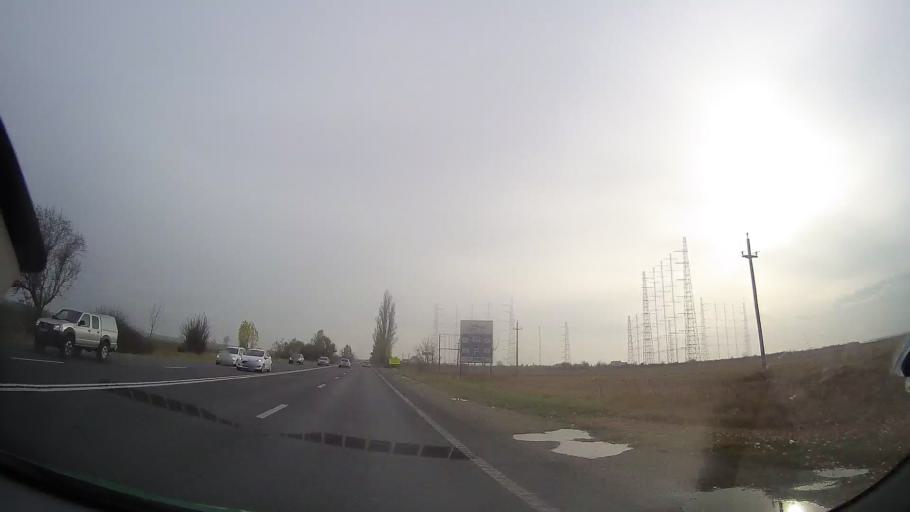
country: RO
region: Prahova
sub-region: Comuna Gorgota
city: Potigrafu
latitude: 44.7561
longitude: 26.1058
